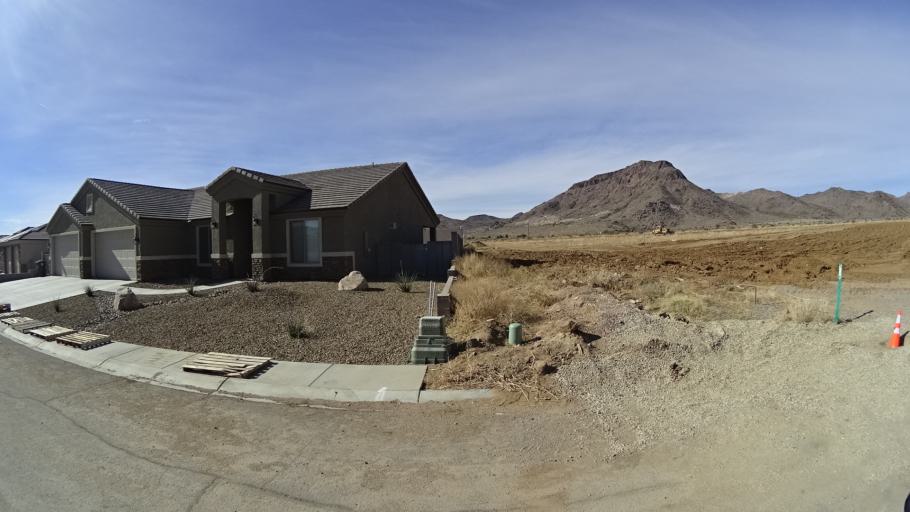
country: US
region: Arizona
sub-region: Mohave County
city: New Kingman-Butler
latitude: 35.2777
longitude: -114.0373
